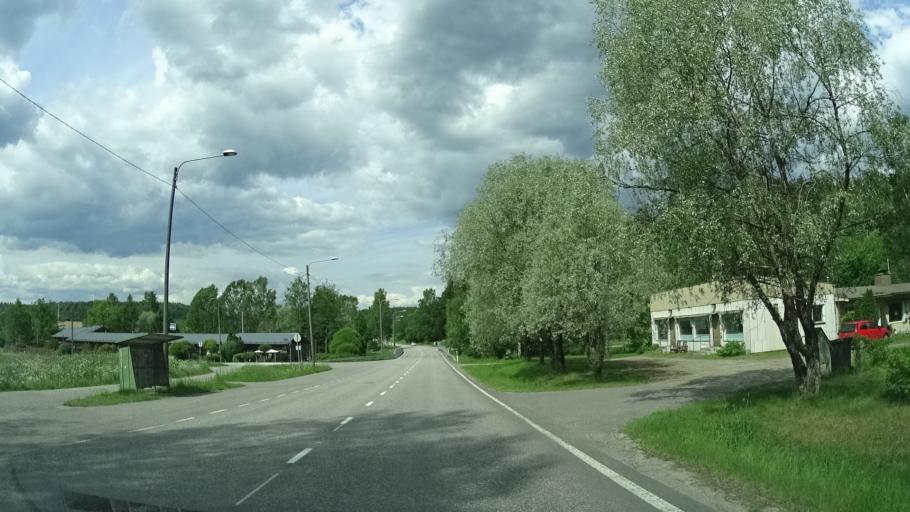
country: FI
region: Uusimaa
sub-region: Helsinki
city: Siuntio
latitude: 60.1778
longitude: 24.2029
